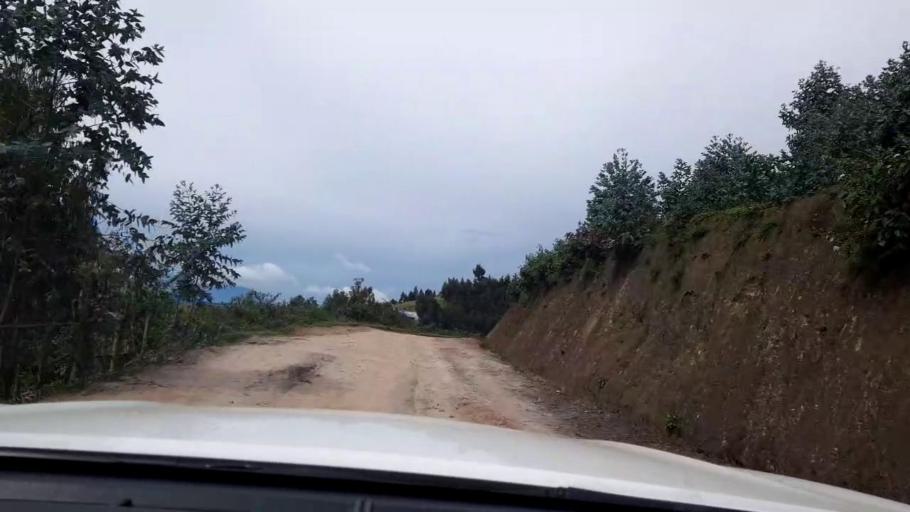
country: RW
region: Western Province
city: Kibuye
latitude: -1.8675
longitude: 29.4510
